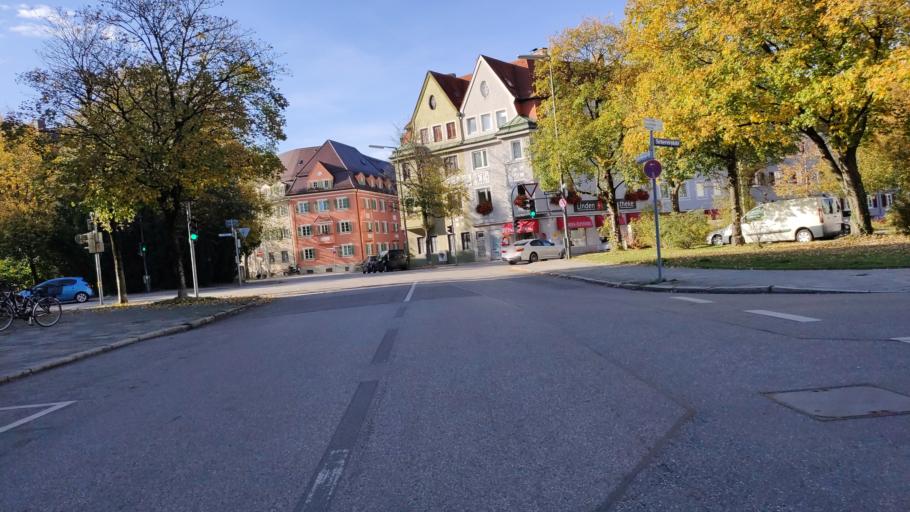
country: DE
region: Bavaria
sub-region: Upper Bavaria
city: Pasing
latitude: 48.1439
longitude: 11.4615
